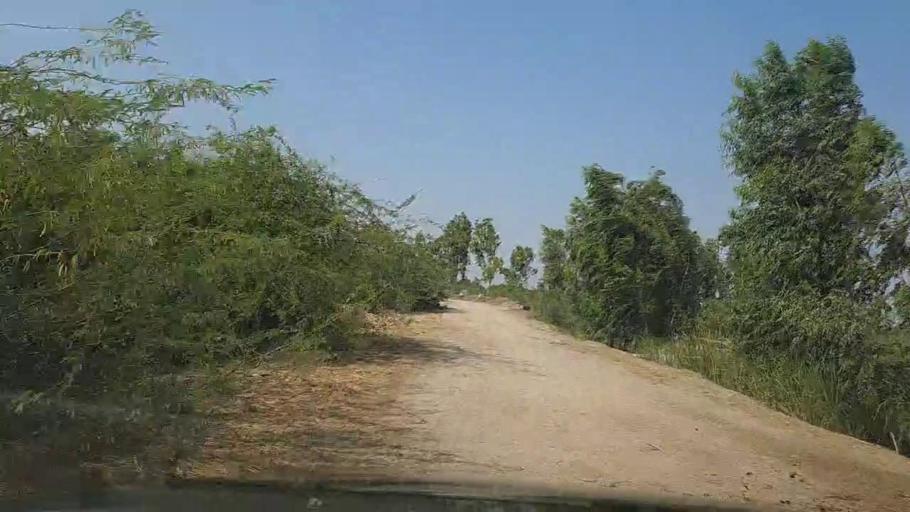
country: PK
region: Sindh
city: Thatta
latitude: 24.6440
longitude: 67.8061
